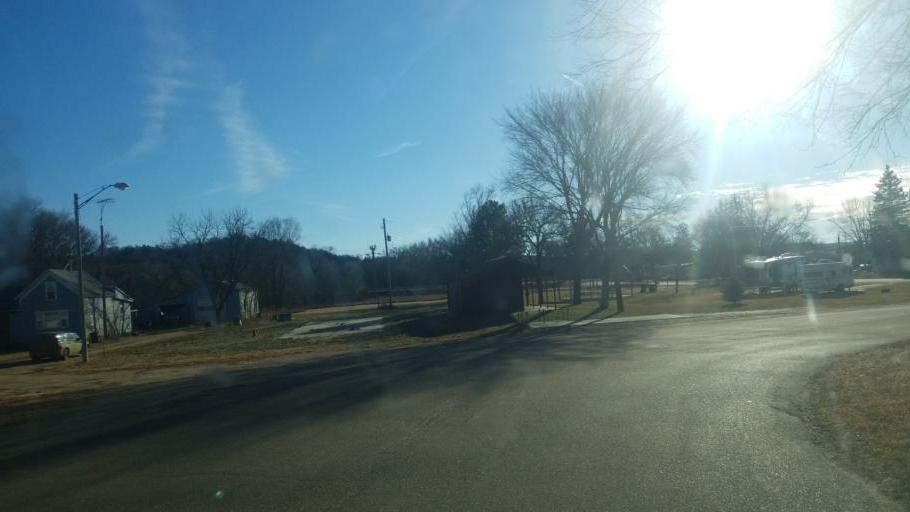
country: US
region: South Dakota
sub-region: Charles Mix County
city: Wagner
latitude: 42.8286
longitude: -98.4663
